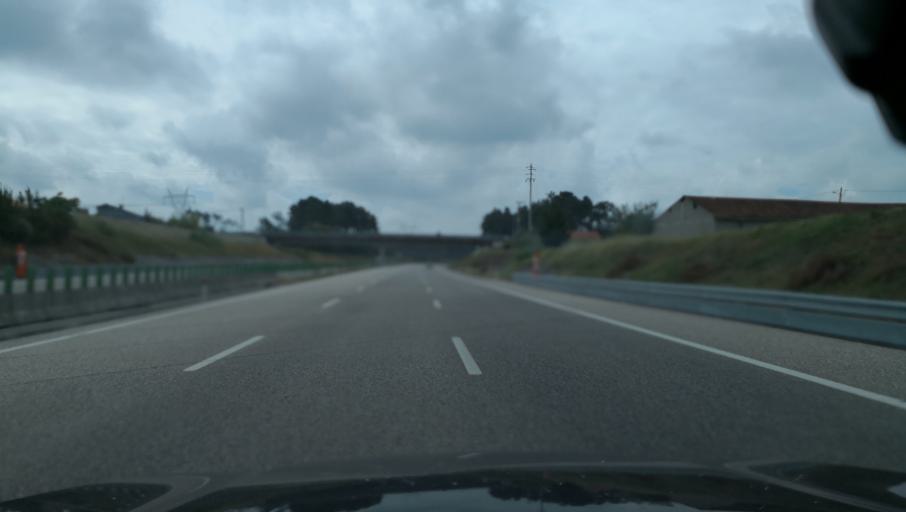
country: PT
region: Leiria
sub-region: Pombal
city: Lourical
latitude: 39.9683
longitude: -8.7801
